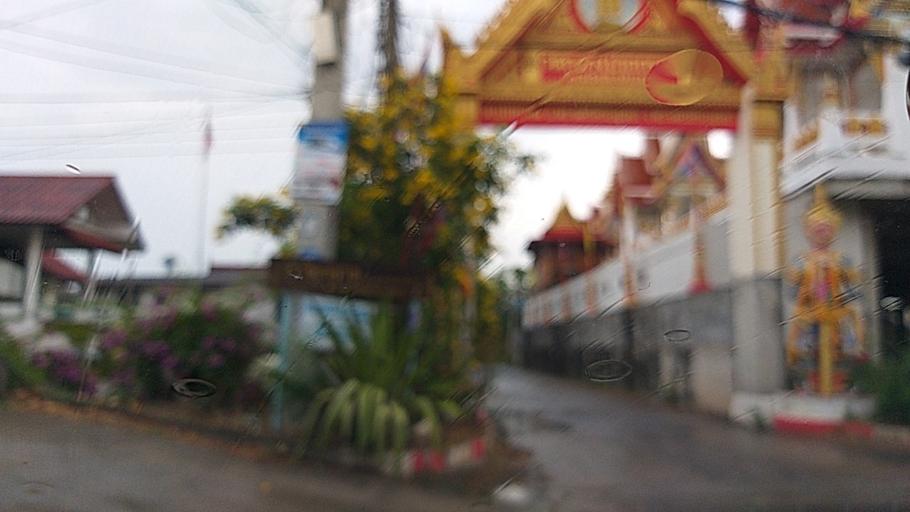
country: TH
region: Phra Nakhon Si Ayutthaya
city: Phra Nakhon Si Ayutthaya
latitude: 14.3382
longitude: 100.5466
